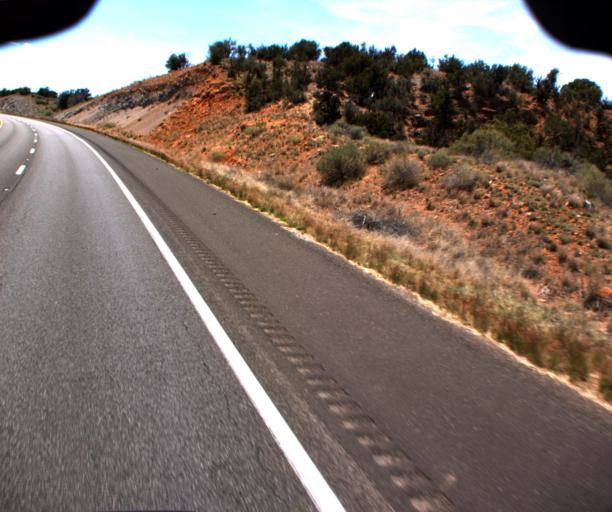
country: US
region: Arizona
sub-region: Yavapai County
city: West Sedona
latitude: 34.8382
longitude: -111.8861
